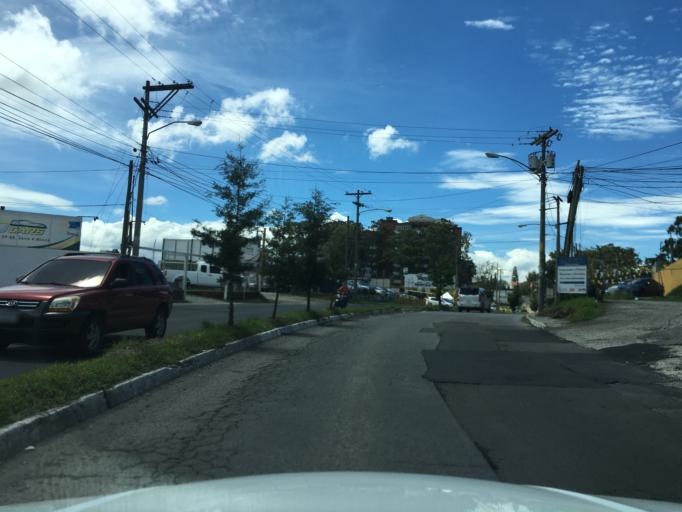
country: GT
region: Guatemala
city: Guatemala City
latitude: 14.6439
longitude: -90.5570
